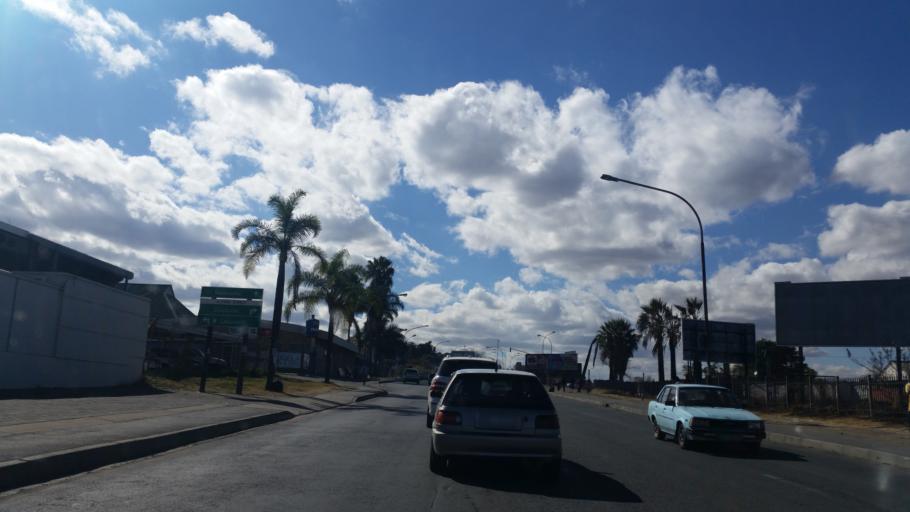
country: ZA
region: KwaZulu-Natal
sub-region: uThukela District Municipality
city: Ladysmith
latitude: -28.5547
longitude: 29.7859
